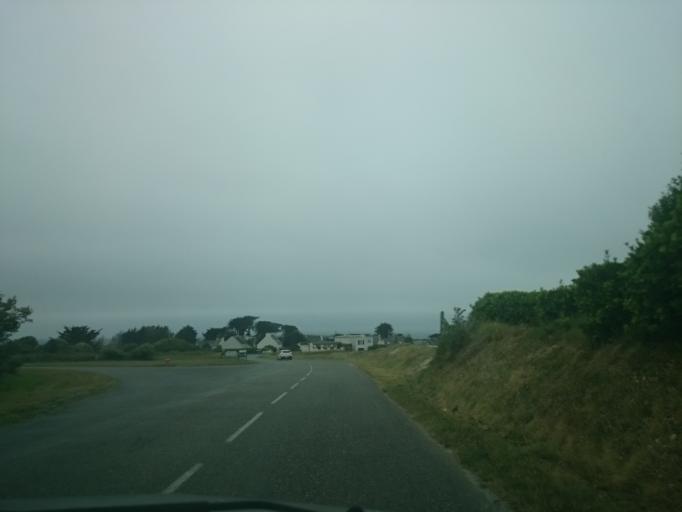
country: FR
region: Brittany
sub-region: Departement du Finistere
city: Saint-Pabu
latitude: 48.5720
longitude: -4.6261
